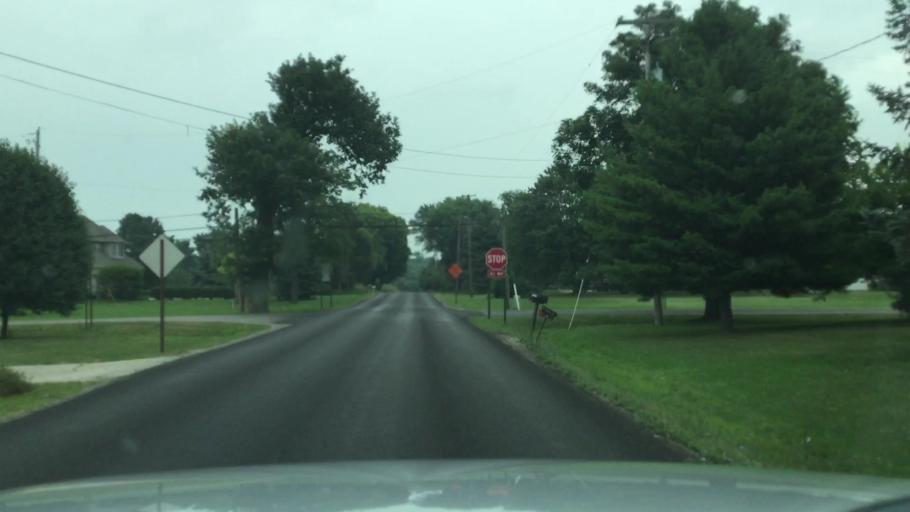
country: US
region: Michigan
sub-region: Shiawassee County
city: New Haven
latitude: 43.0569
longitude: -84.1868
